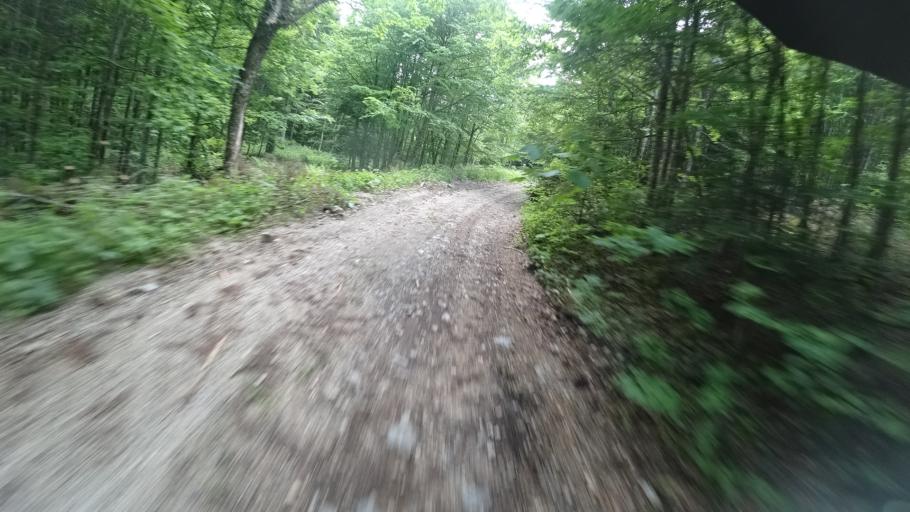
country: HR
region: Zadarska
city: Gracac
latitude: 44.4849
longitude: 15.8784
